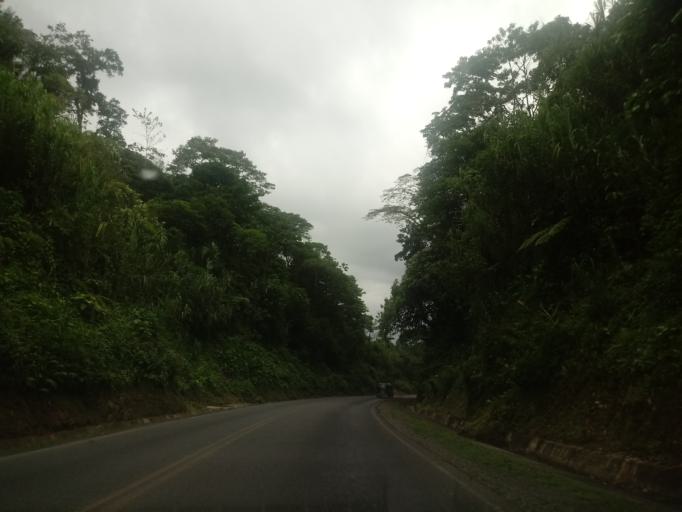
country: CR
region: San Jose
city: Dulce Nombre de Jesus
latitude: 10.1583
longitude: -83.9393
